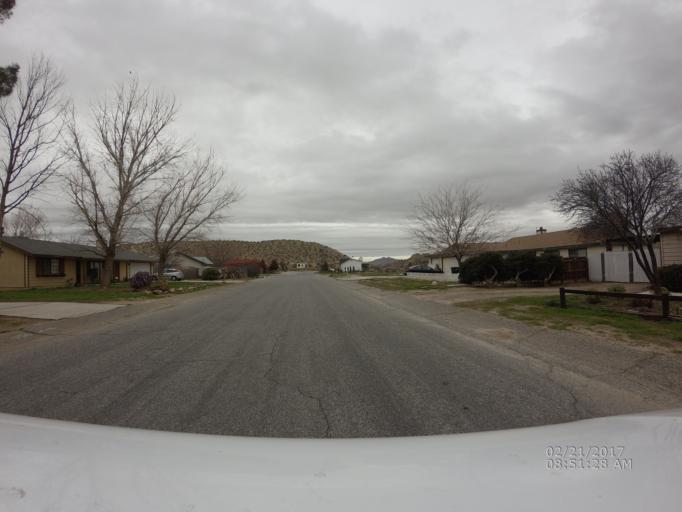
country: US
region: California
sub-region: Los Angeles County
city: Lake Los Angeles
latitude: 34.5973
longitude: -117.8278
